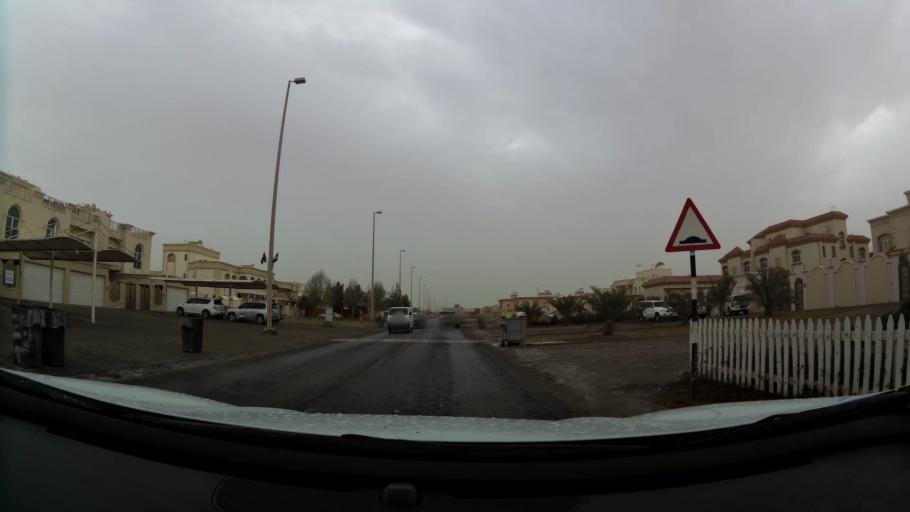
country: AE
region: Abu Dhabi
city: Abu Dhabi
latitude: 24.4157
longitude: 54.5852
